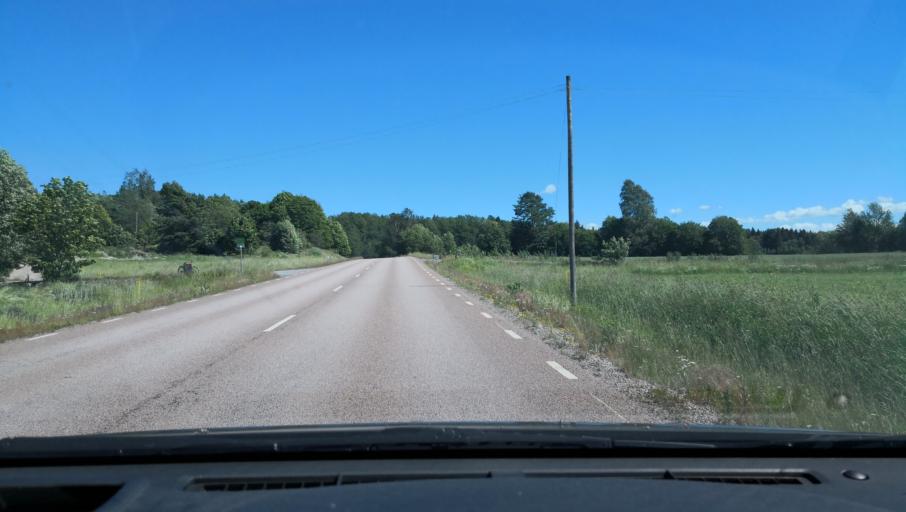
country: SE
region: Vaestmanland
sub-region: Kungsors Kommun
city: Kungsoer
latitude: 59.2888
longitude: 16.1015
